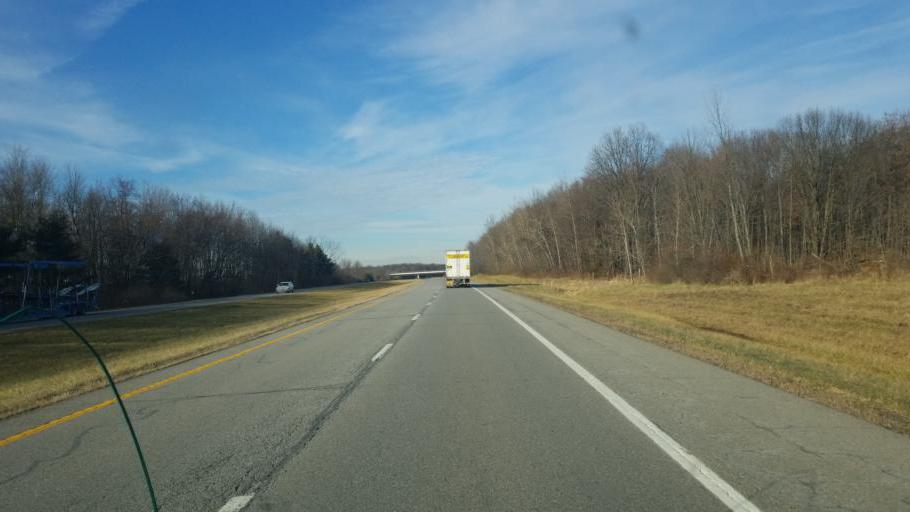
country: US
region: Ohio
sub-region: Trumbull County
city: Cortland
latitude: 41.4844
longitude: -80.7121
